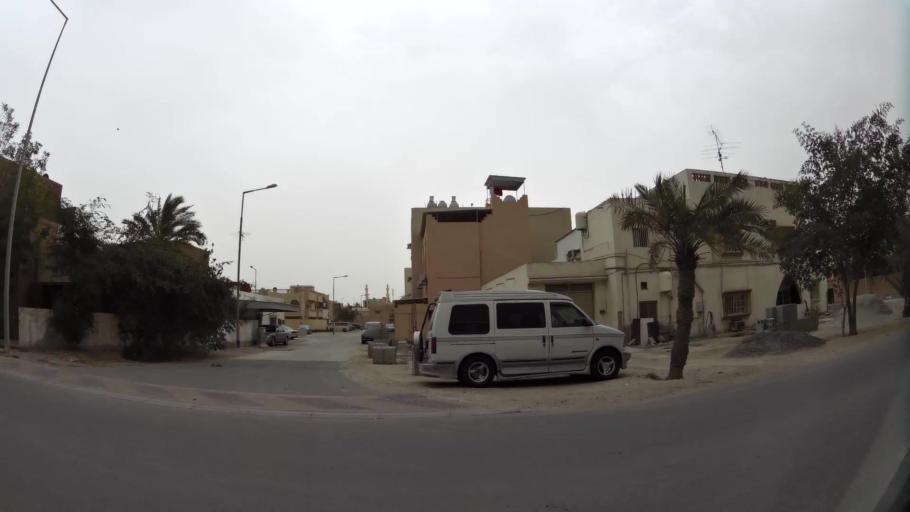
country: BH
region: Northern
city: Madinat `Isa
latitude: 26.1712
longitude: 50.5436
